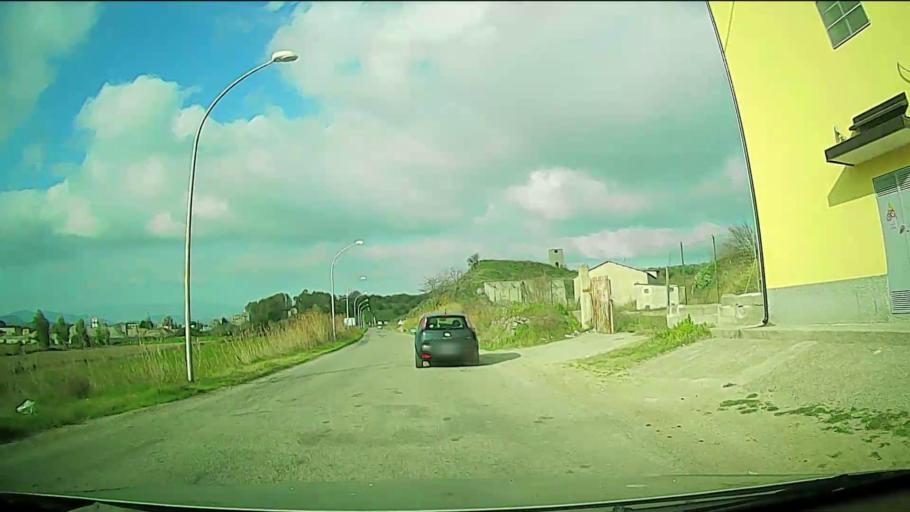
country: IT
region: Calabria
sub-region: Provincia di Crotone
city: Rocca di Neto
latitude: 39.1806
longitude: 17.0240
